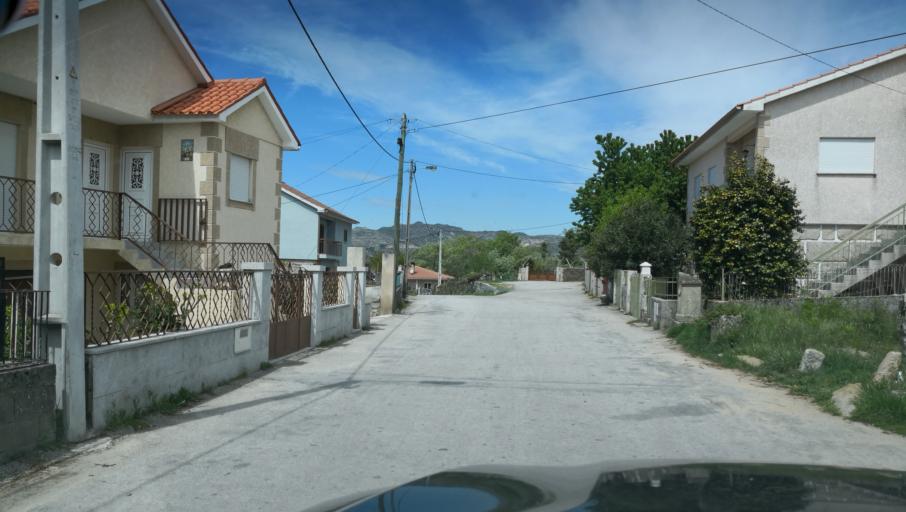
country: PT
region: Vila Real
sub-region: Vila Real
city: Vila Real
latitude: 41.3606
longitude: -7.6666
